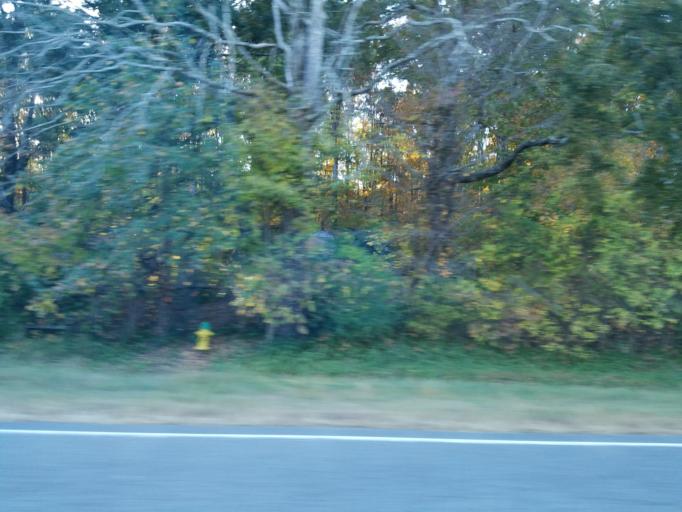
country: US
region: Georgia
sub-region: Bartow County
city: Adairsville
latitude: 34.3124
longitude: -84.9373
